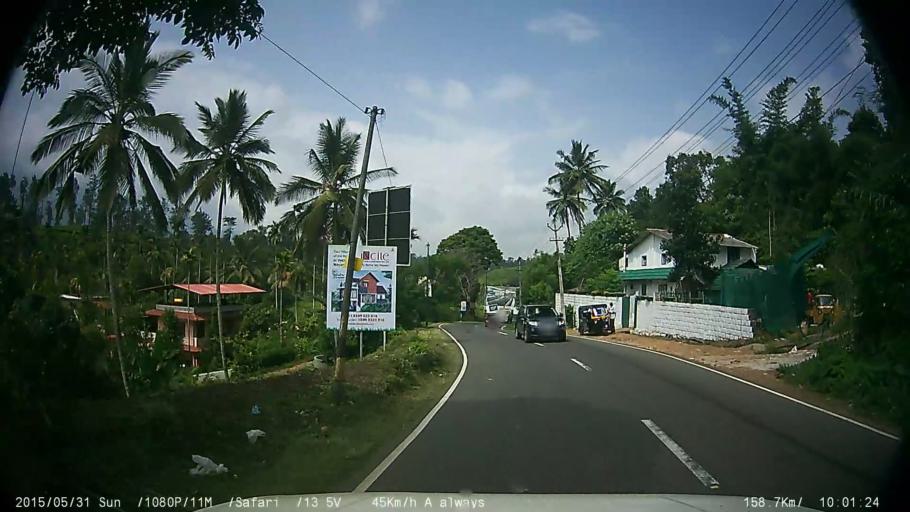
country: IN
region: Kerala
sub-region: Wayanad
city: Kalpetta
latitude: 11.5803
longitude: 76.0622
